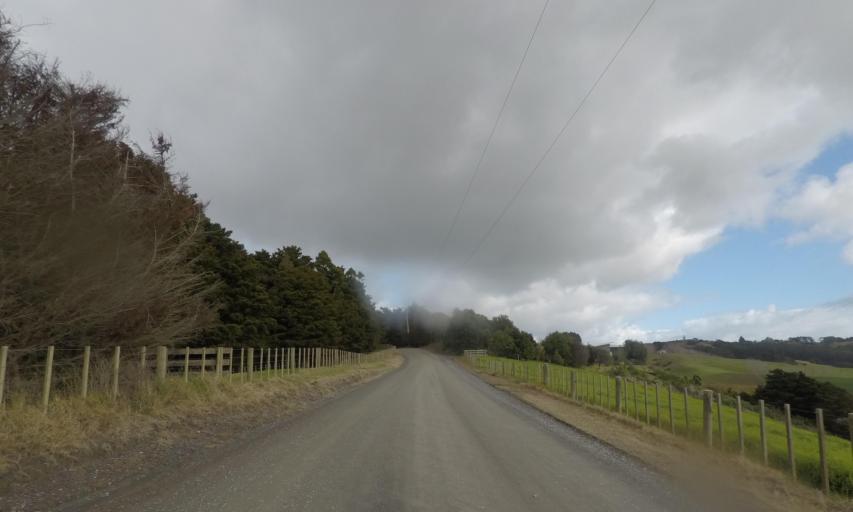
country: NZ
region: Auckland
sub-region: Auckland
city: Wellsford
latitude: -36.1687
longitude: 174.6024
